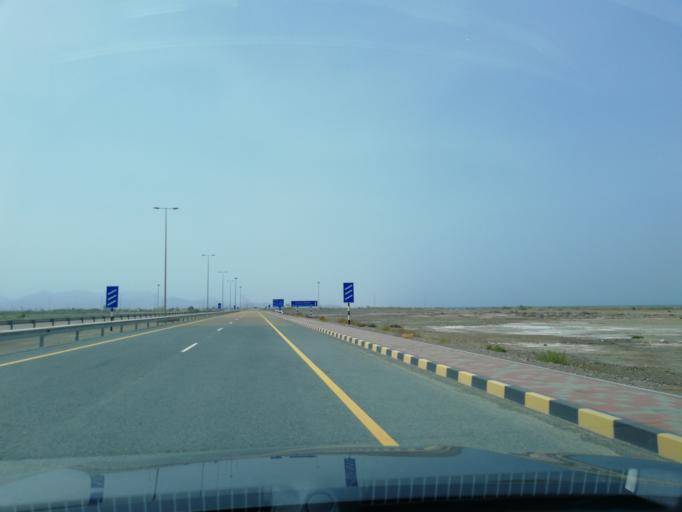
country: OM
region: Al Batinah
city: Shinas
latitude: 24.8607
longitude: 56.4150
